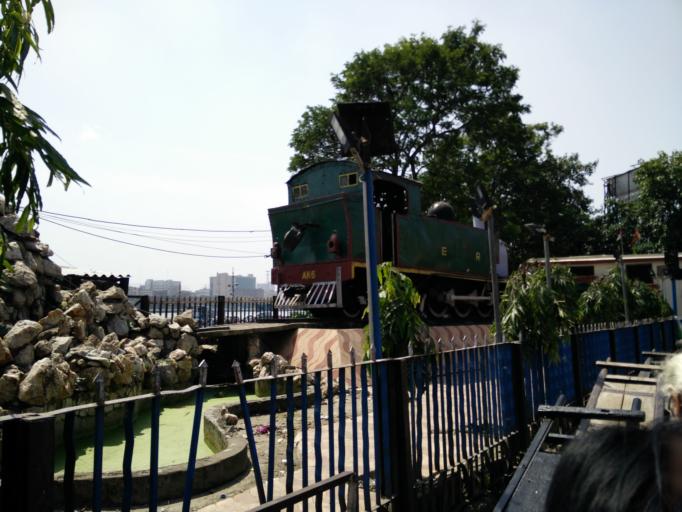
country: IN
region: West Bengal
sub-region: Kolkata
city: Bara Bazar
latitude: 22.5838
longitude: 88.3439
